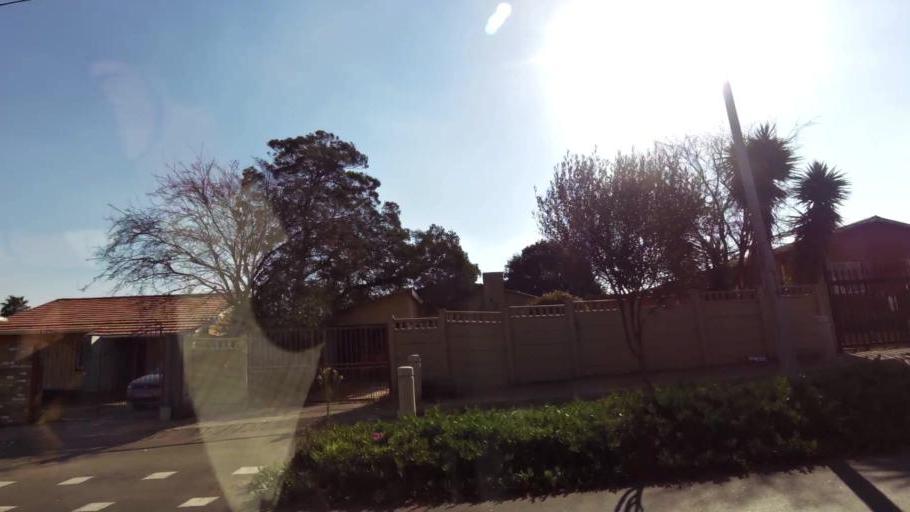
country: ZA
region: Gauteng
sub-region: City of Johannesburg Metropolitan Municipality
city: Johannesburg
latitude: -26.1772
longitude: 27.9775
